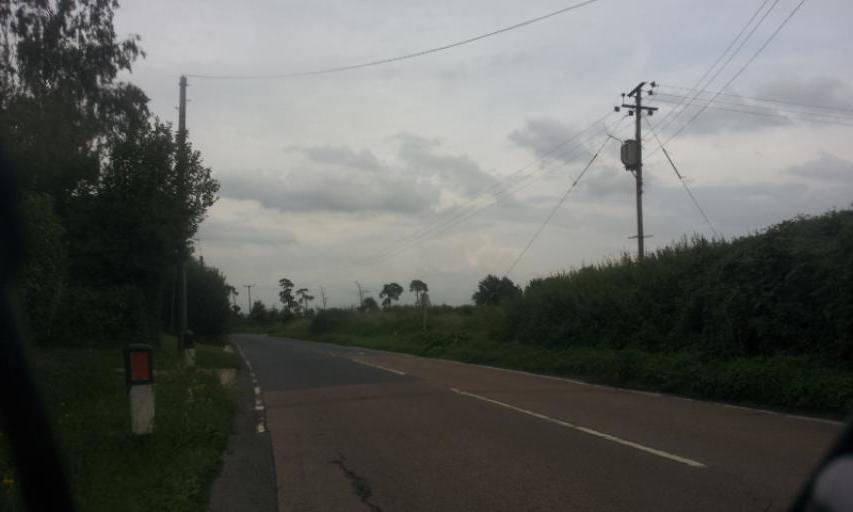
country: GB
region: England
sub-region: Kent
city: East Peckham
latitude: 51.2066
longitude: 0.3656
